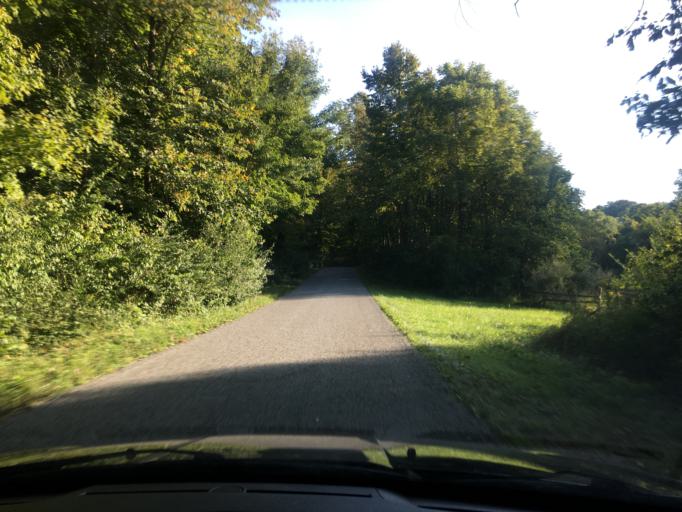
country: US
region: Ohio
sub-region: Logan County
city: West Liberty
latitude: 40.2580
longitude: -83.6624
